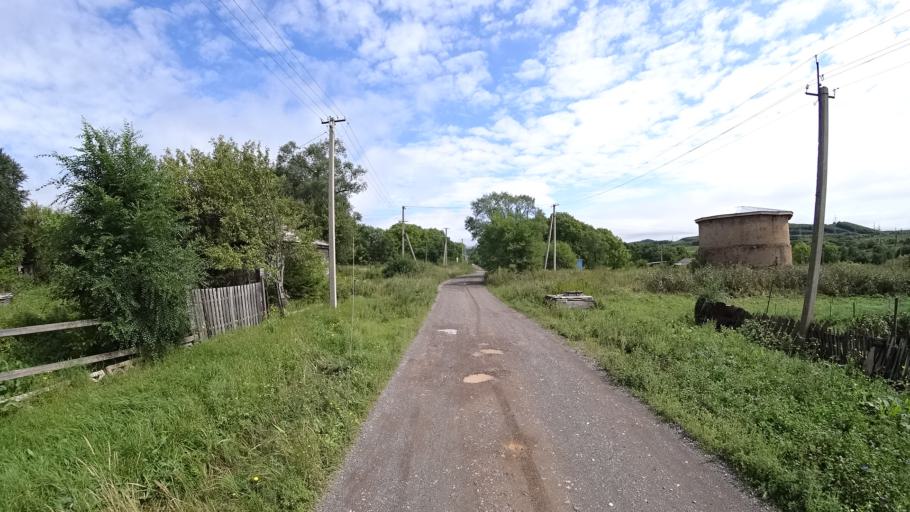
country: RU
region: Primorskiy
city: Lyalichi
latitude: 44.1382
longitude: 132.3868
